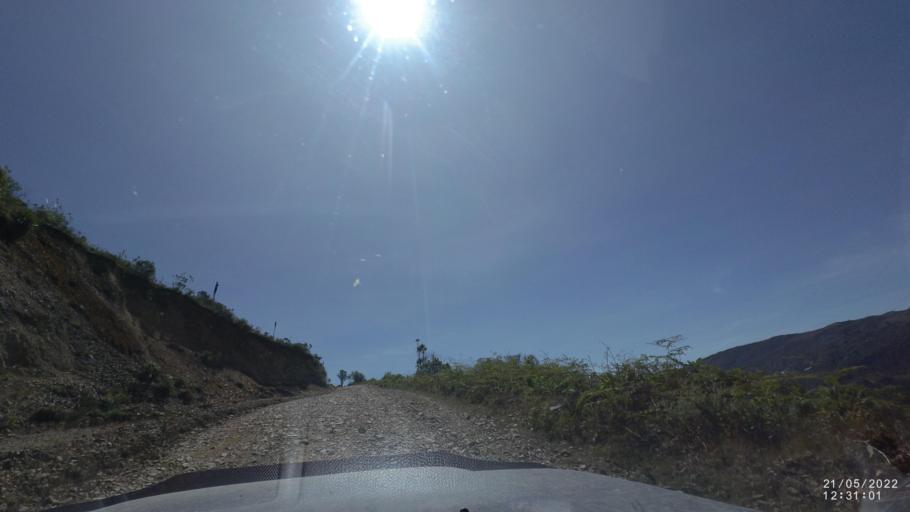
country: BO
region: Cochabamba
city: Colomi
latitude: -17.2132
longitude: -65.9128
